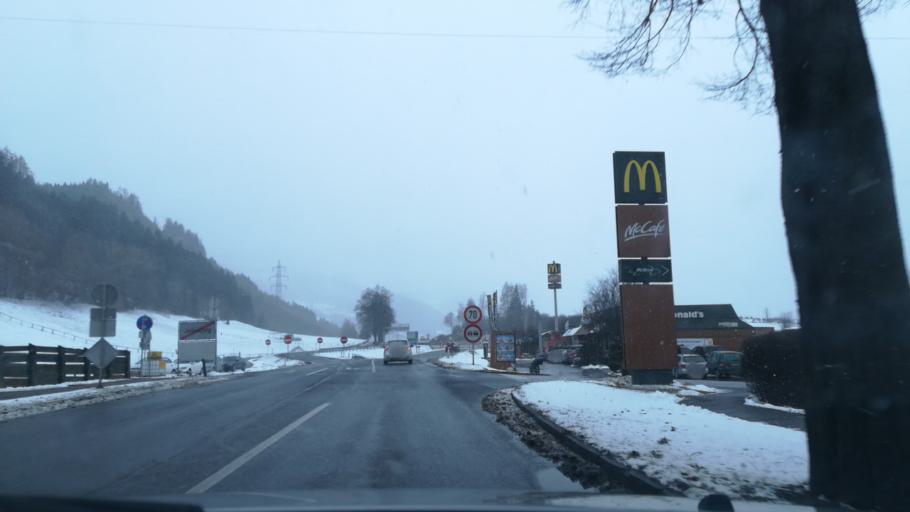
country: AT
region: Styria
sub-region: Politischer Bezirk Murtal
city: Oberweg
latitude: 47.1718
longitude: 14.6326
